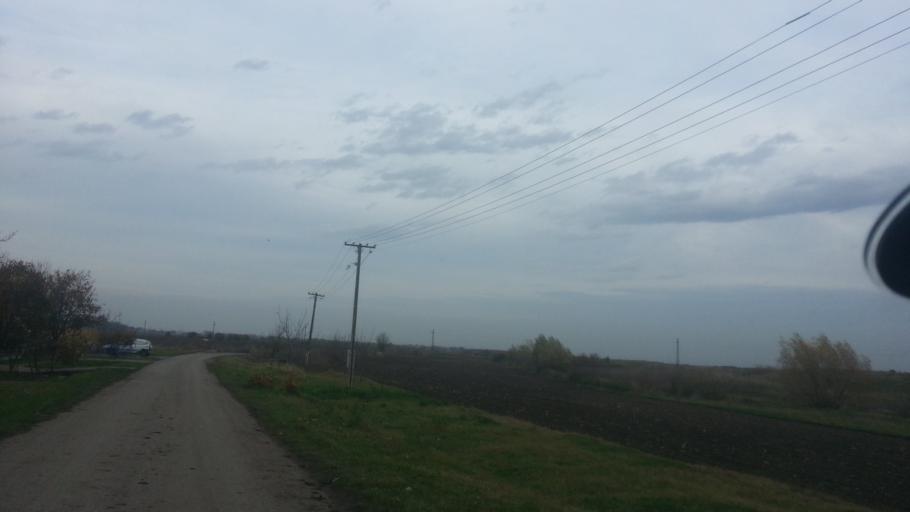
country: RS
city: Putinci
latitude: 44.9712
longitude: 19.9696
